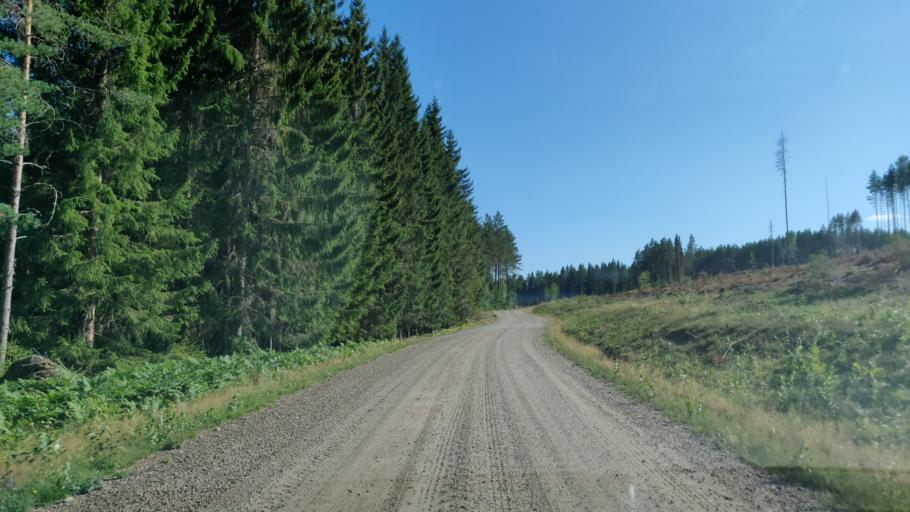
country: SE
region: Vaermland
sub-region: Hagfors Kommun
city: Ekshaerad
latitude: 60.1487
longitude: 13.5169
